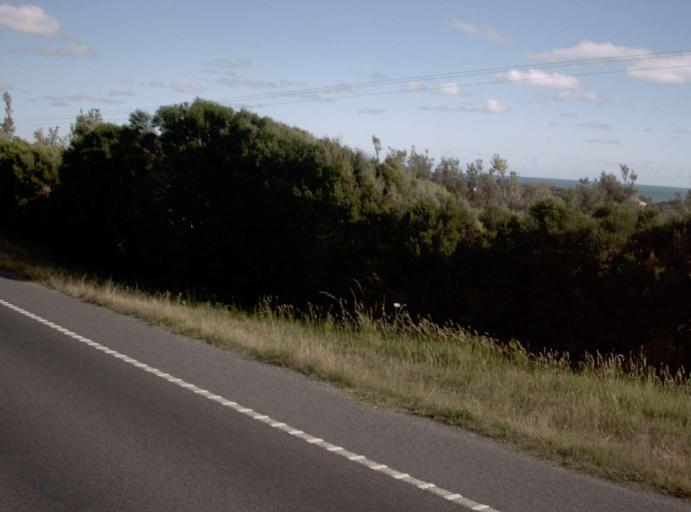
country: AU
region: Victoria
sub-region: Bass Coast
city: North Wonthaggi
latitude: -38.5599
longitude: 145.4946
